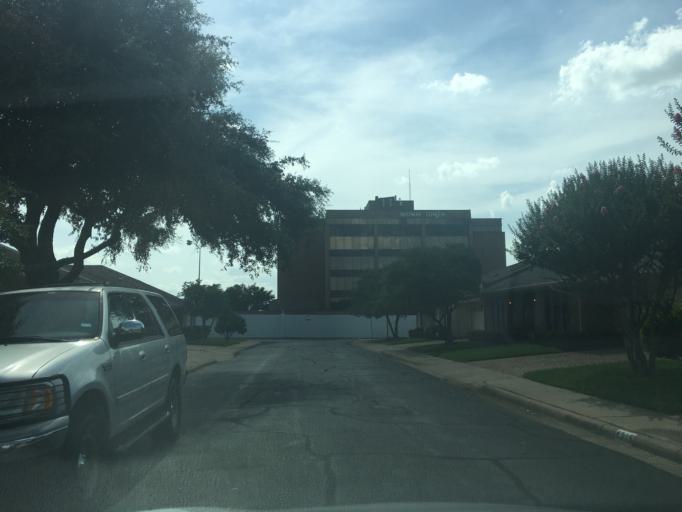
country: US
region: Texas
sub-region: Dallas County
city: Addison
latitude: 32.9236
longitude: -96.8351
